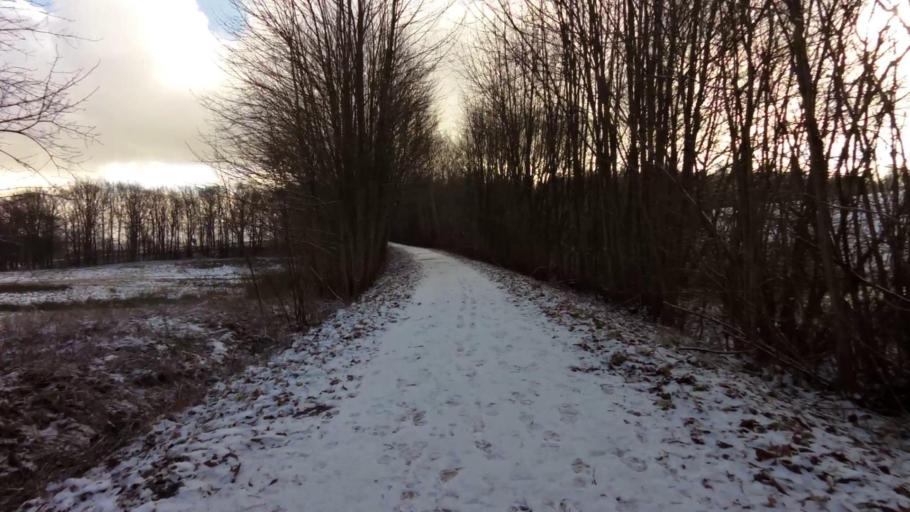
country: PL
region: West Pomeranian Voivodeship
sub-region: Powiat swidwinski
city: Polczyn-Zdroj
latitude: 53.7527
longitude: 16.0578
